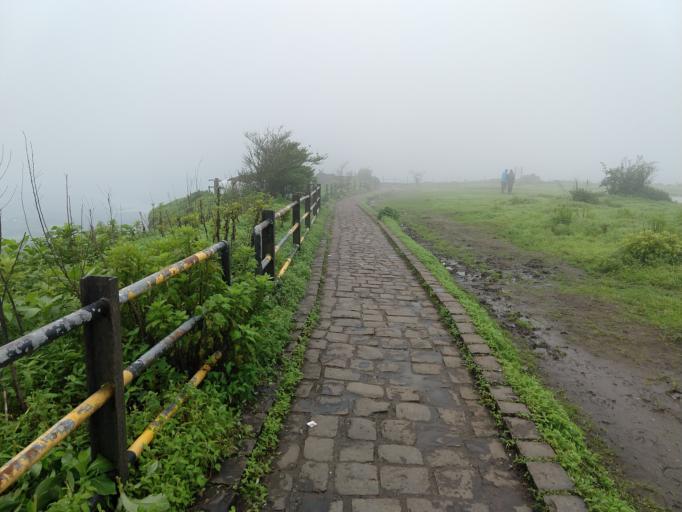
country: IN
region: Maharashtra
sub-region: Pune Division
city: Kharakvasla
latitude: 18.3662
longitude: 73.7520
